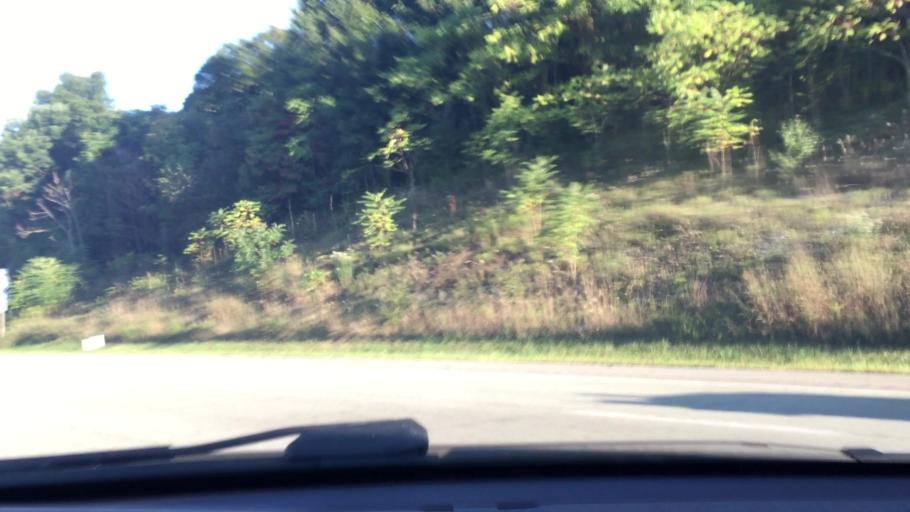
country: US
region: Pennsylvania
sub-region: Washington County
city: Cecil-Bishop
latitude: 40.2987
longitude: -80.1645
